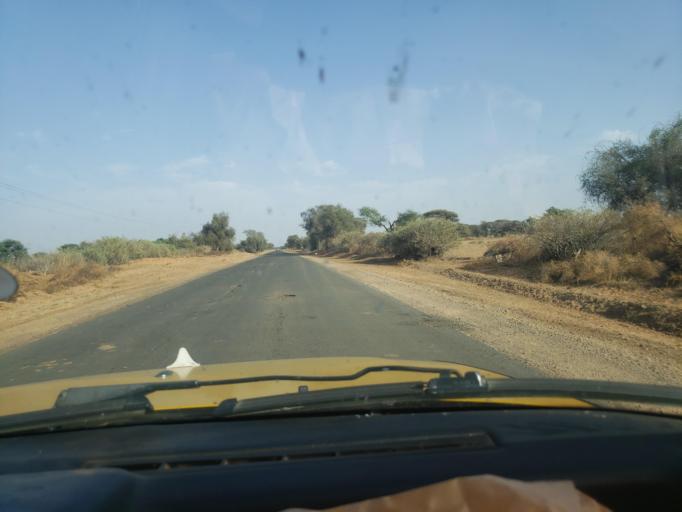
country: SN
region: Louga
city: Louga
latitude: 15.5088
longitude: -15.9757
